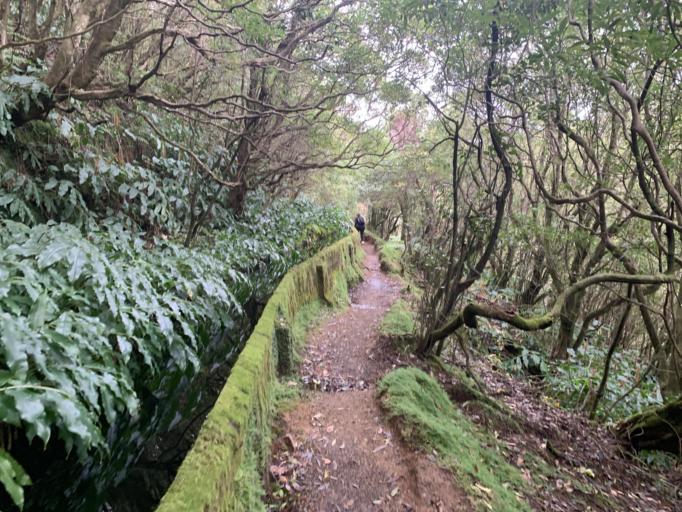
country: PT
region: Azores
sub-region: Vila Franca do Campo
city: Vila Franca do Campo
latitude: 37.7423
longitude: -25.4742
